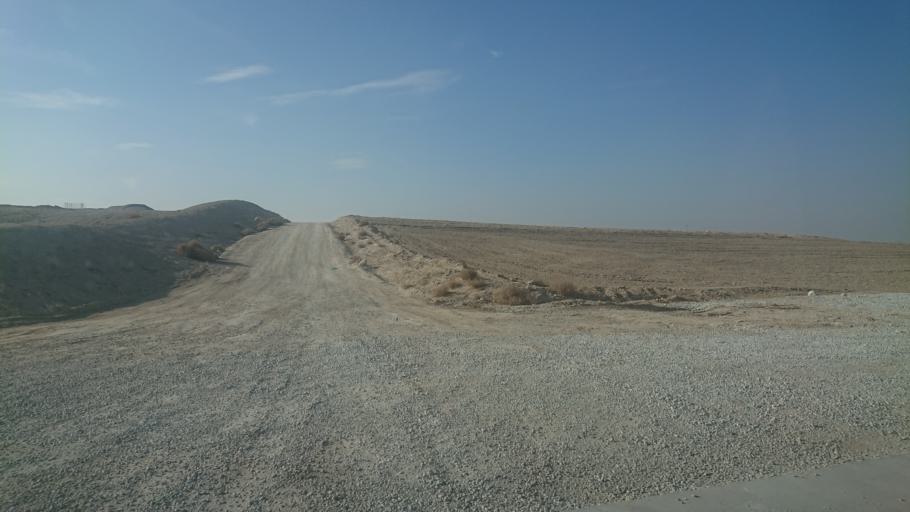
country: TR
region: Aksaray
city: Sultanhani
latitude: 38.0674
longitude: 33.6216
